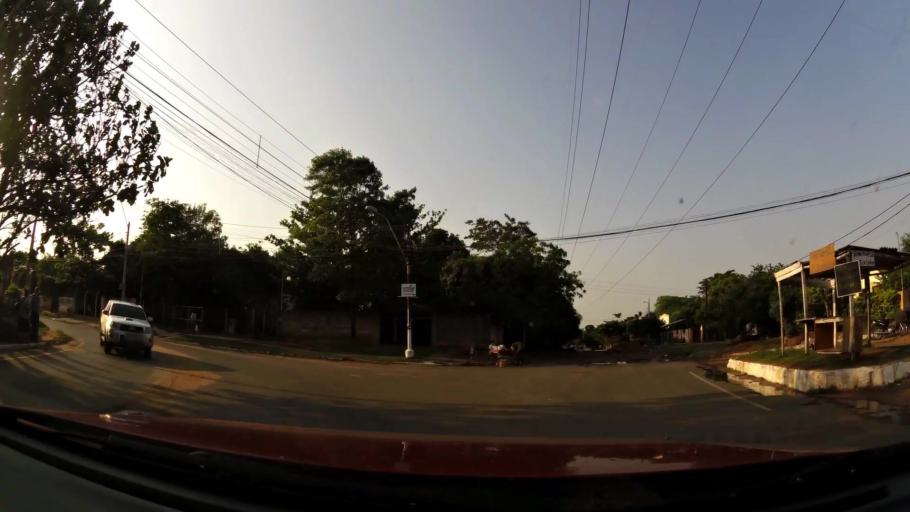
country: PY
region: Central
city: Lambare
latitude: -25.3547
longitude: -57.6088
